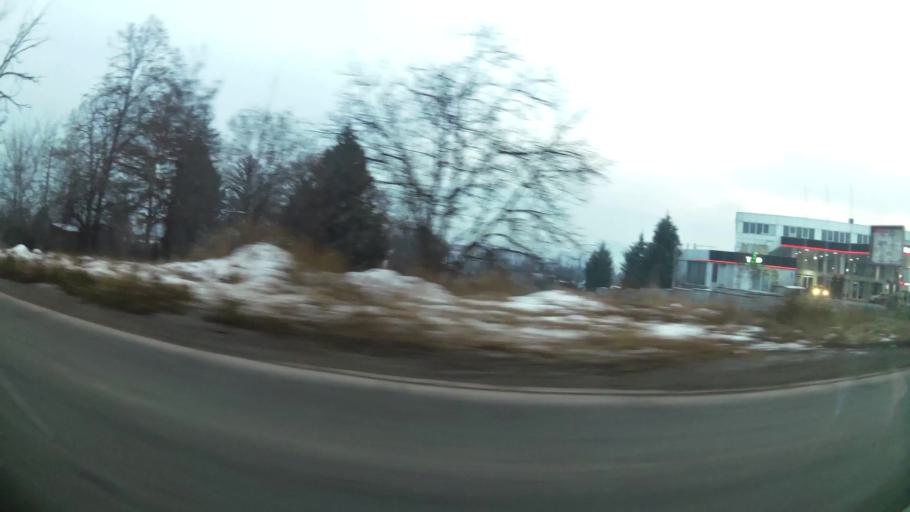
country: MK
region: Suto Orizari
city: Suto Orizare
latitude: 42.0149
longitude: 21.3960
